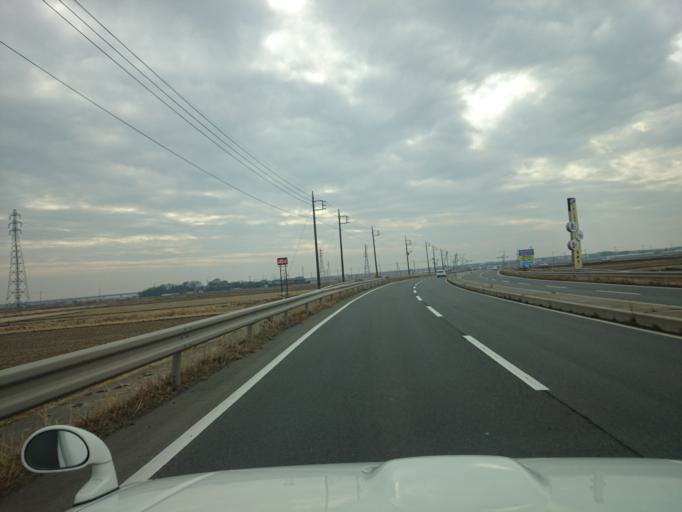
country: JP
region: Ibaraki
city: Ishige
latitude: 36.0912
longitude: 139.9861
